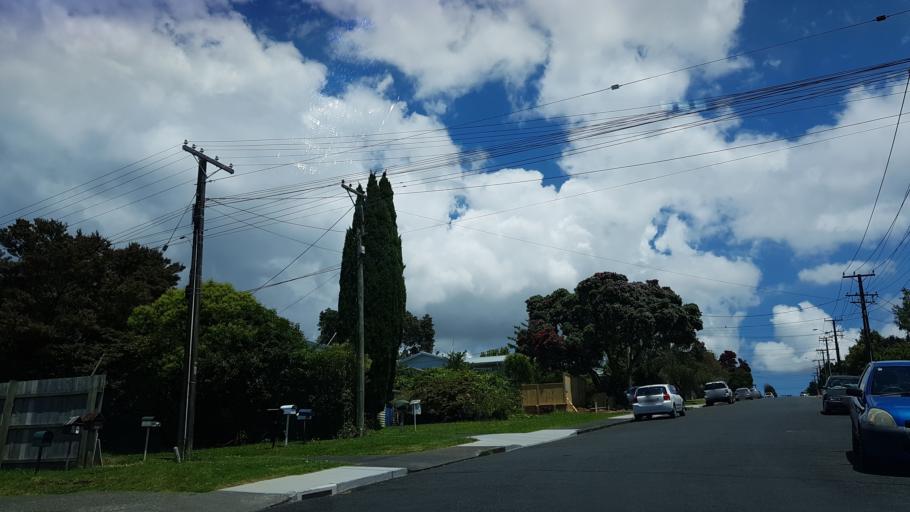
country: NZ
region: Auckland
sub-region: Auckland
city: North Shore
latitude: -36.7971
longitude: 174.6942
